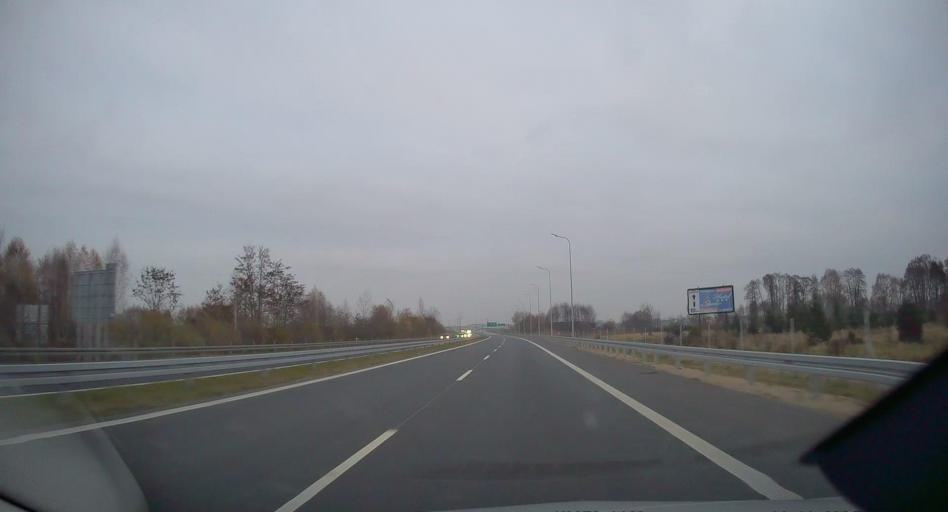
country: PL
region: Silesian Voivodeship
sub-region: Powiat bedzinski
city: Siewierz
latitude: 50.4207
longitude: 19.1932
